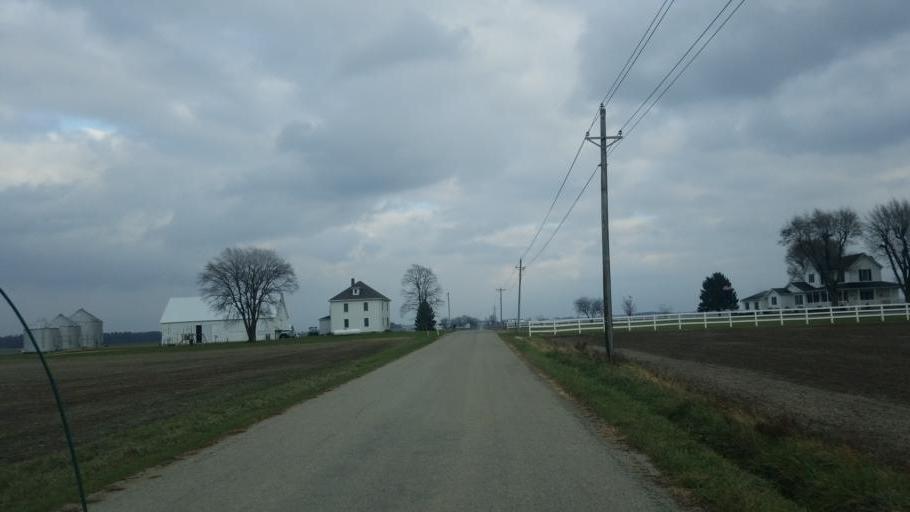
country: US
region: Ohio
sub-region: Mercer County
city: Fort Recovery
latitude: 40.5135
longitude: -84.8275
